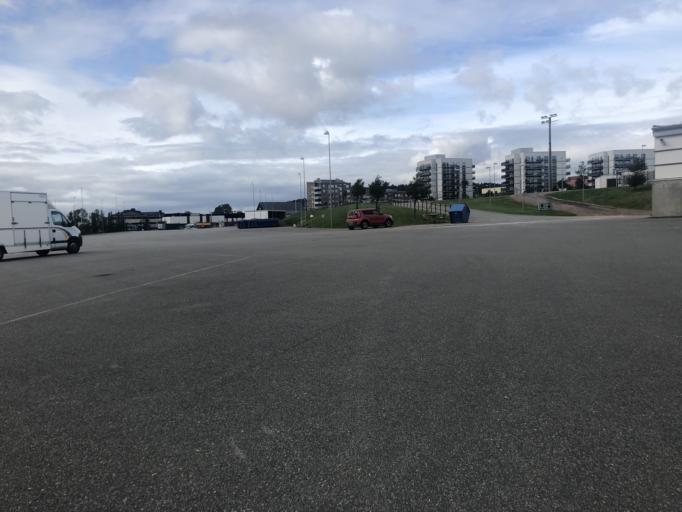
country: SE
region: Vaestra Goetaland
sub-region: Molndal
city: Moelndal
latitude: 57.6488
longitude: 12.0000
